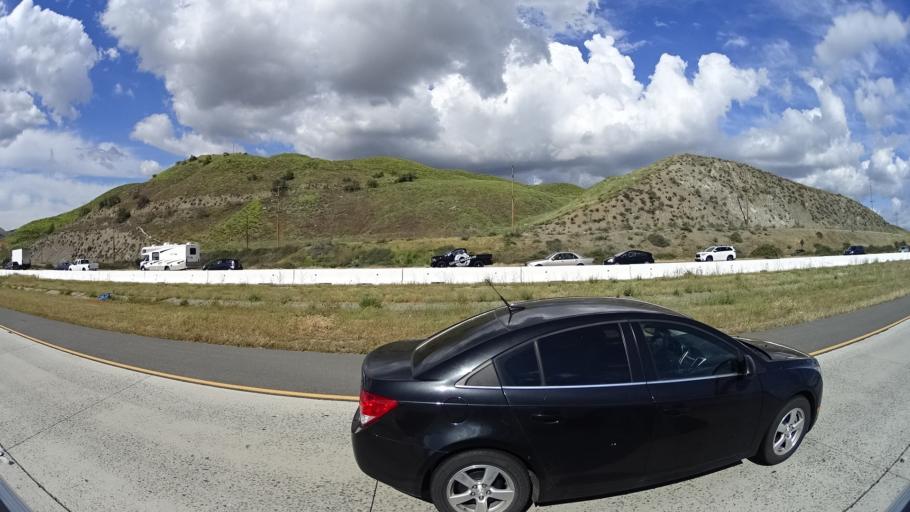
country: US
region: California
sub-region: Riverside County
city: Lake Elsinore
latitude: 33.6762
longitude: -117.3225
